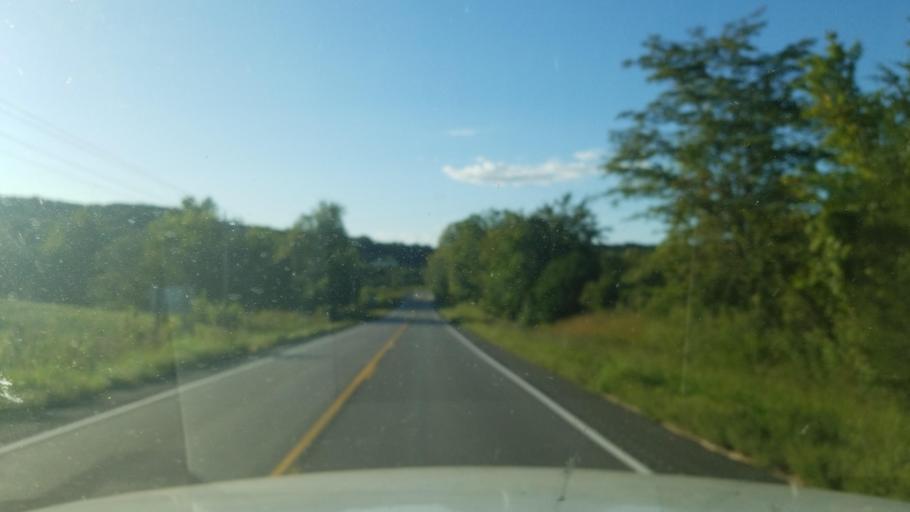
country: US
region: Illinois
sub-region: Hardin County
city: Rosiclare
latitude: 37.5652
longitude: -88.4101
